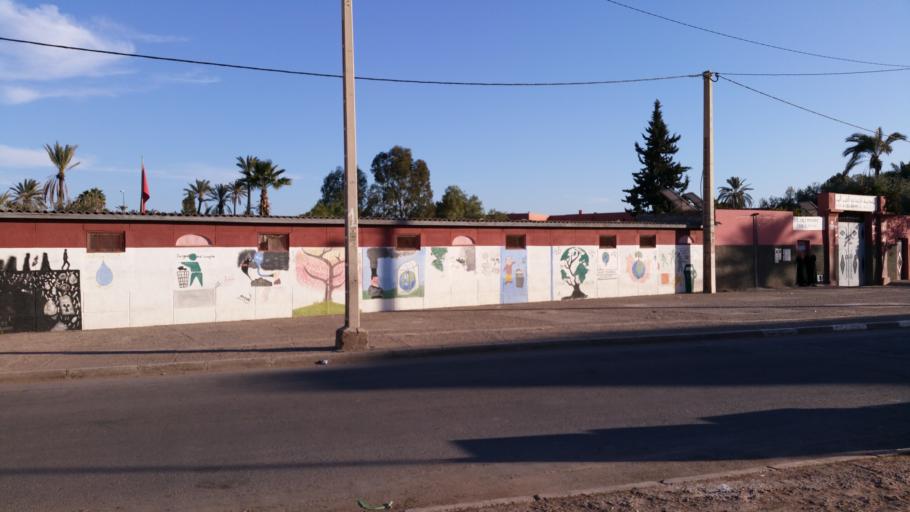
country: MA
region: Marrakech-Tensift-Al Haouz
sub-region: Marrakech
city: Marrakesh
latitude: 31.6483
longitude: -7.9787
